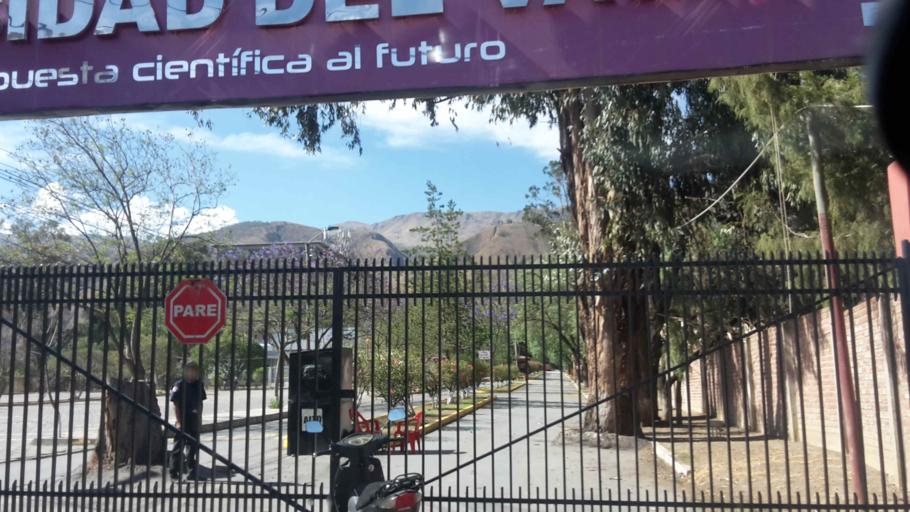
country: BO
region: Cochabamba
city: Cochabamba
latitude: -17.3342
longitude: -66.2259
